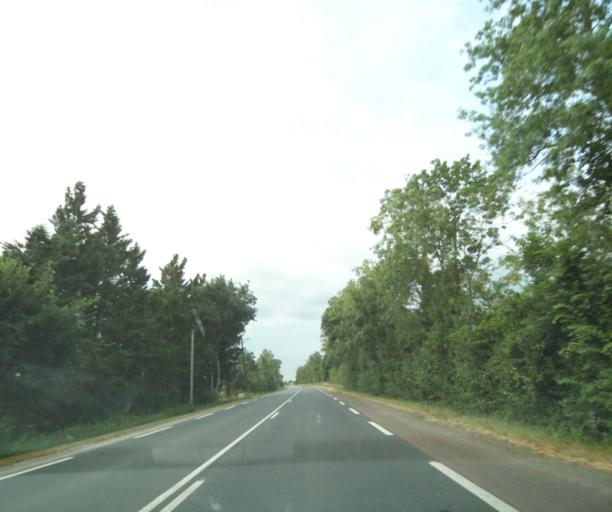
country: FR
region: Poitou-Charentes
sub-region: Departement de la Charente-Maritime
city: Marans
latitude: 46.3475
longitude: -0.9969
